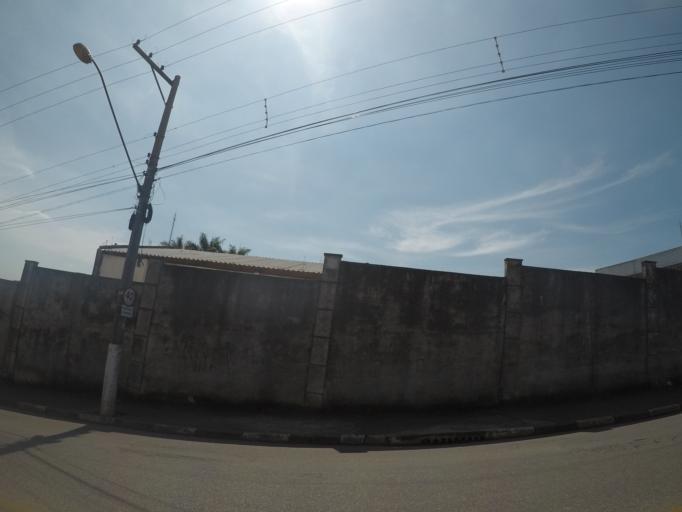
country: BR
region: Sao Paulo
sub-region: Cabreuva
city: Cabreuva
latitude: -23.2603
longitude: -47.0565
